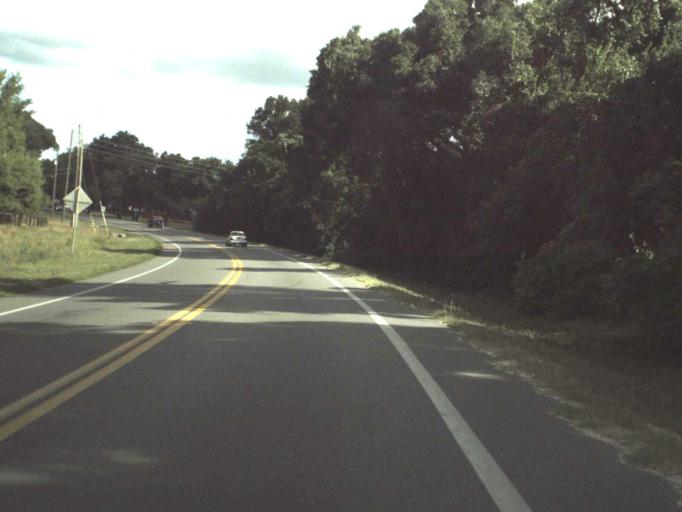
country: US
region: Florida
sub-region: Marion County
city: Belleview
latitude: 29.0678
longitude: -82.0534
